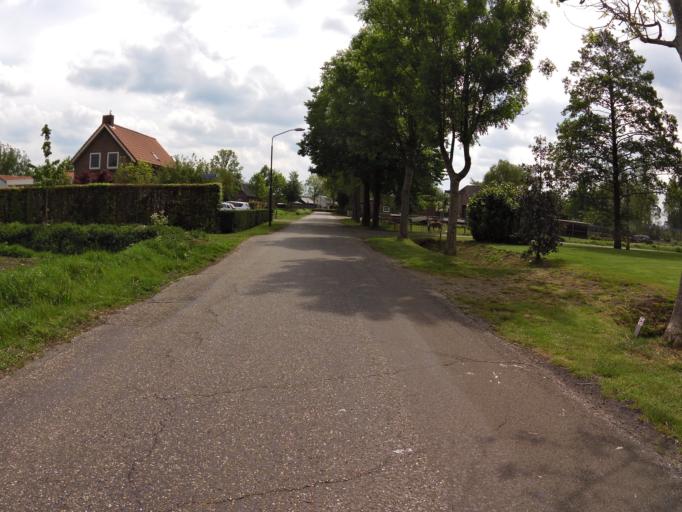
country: NL
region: North Brabant
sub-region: Gemeente Boxtel
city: Boxtel
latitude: 51.6079
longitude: 5.3459
